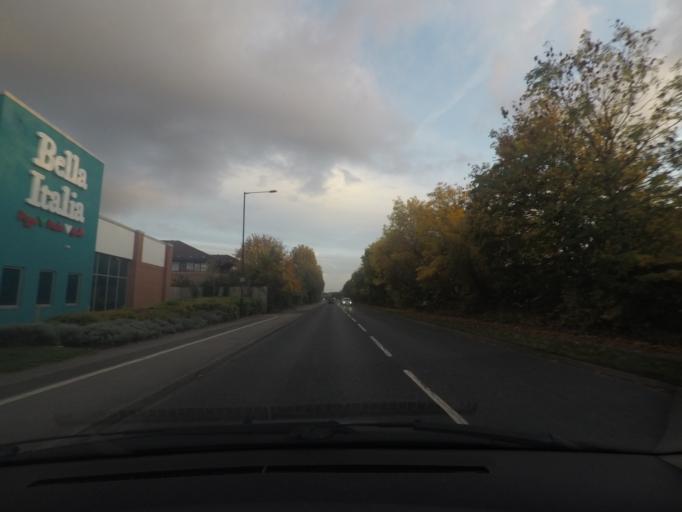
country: GB
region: England
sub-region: City of York
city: Skelton
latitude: 53.9896
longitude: -1.1052
